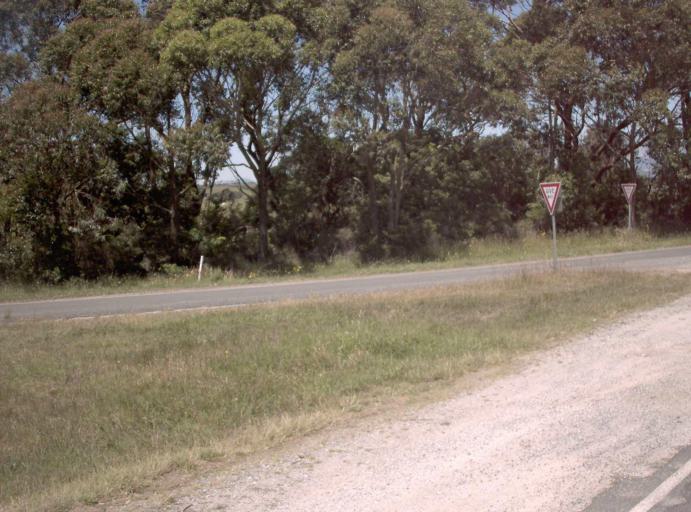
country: AU
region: Victoria
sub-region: Bass Coast
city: North Wonthaggi
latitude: -38.7658
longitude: 146.0622
